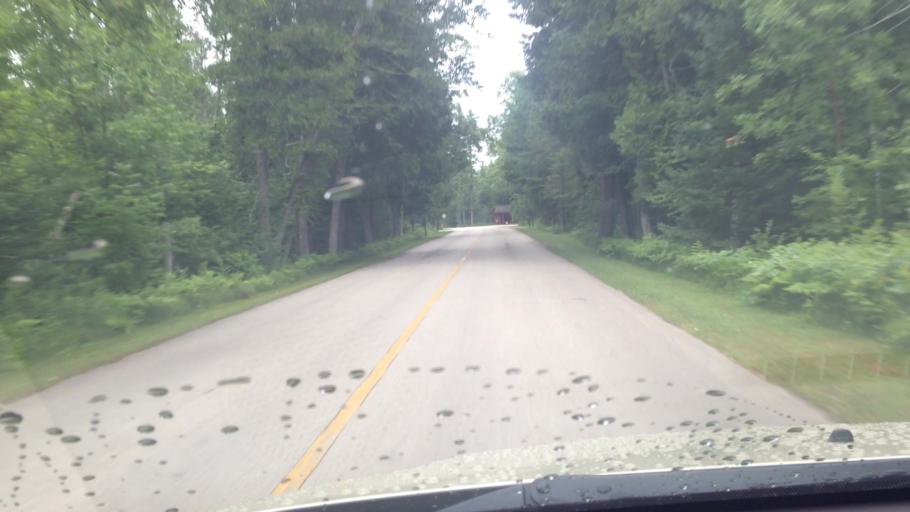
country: US
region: Michigan
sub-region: Menominee County
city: Menominee
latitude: 45.3906
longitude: -87.3674
